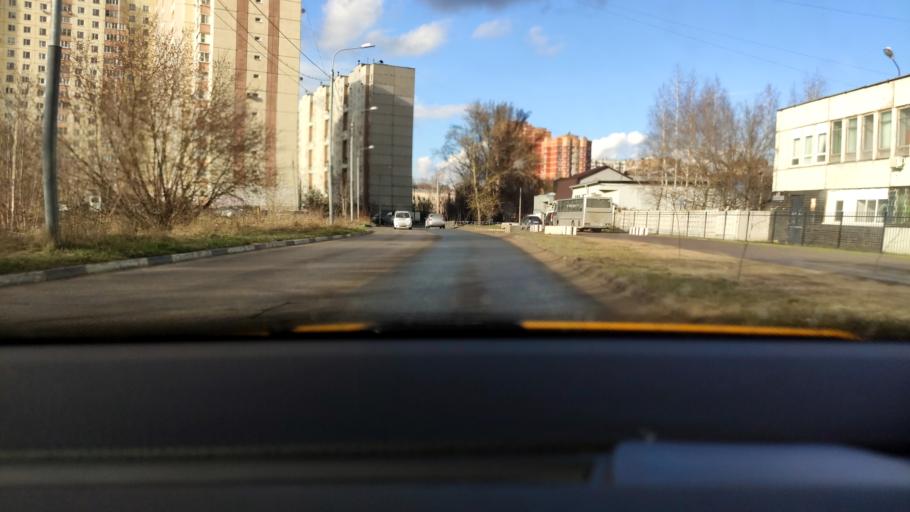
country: RU
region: Moskovskaya
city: Saltykovka
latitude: 55.7457
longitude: 37.9485
